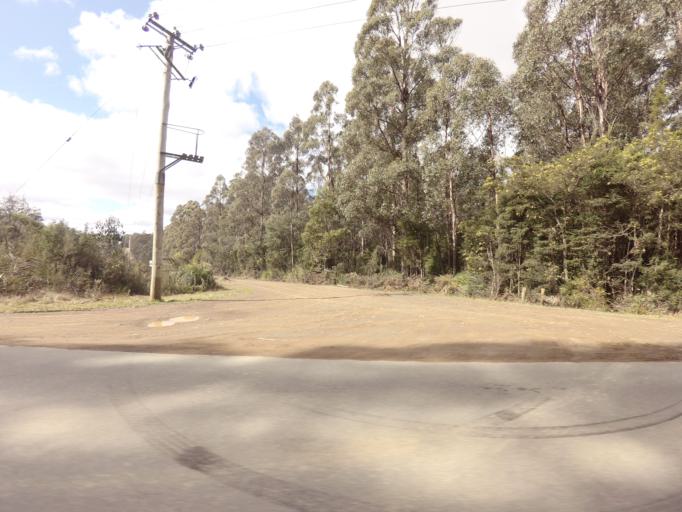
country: AU
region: Tasmania
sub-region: Huon Valley
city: Geeveston
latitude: -43.3569
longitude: 146.9589
